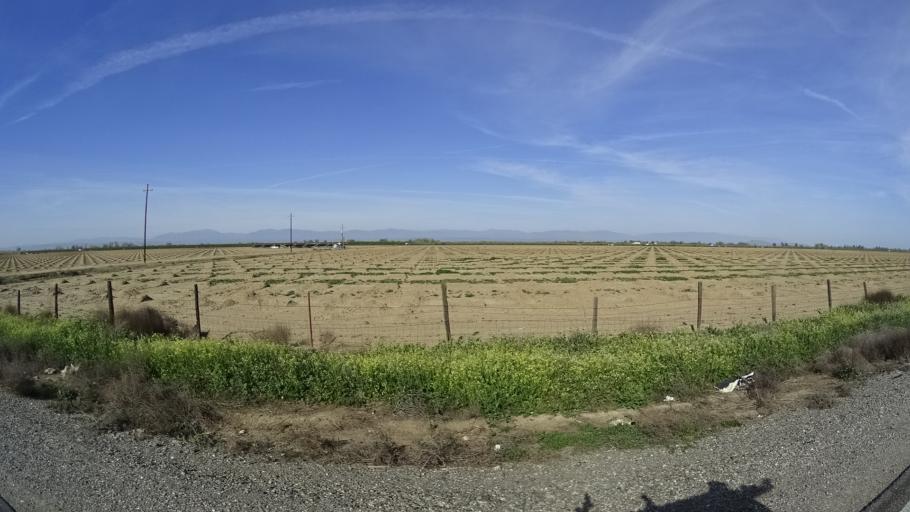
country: US
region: California
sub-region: Glenn County
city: Orland
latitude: 39.6538
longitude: -122.1972
